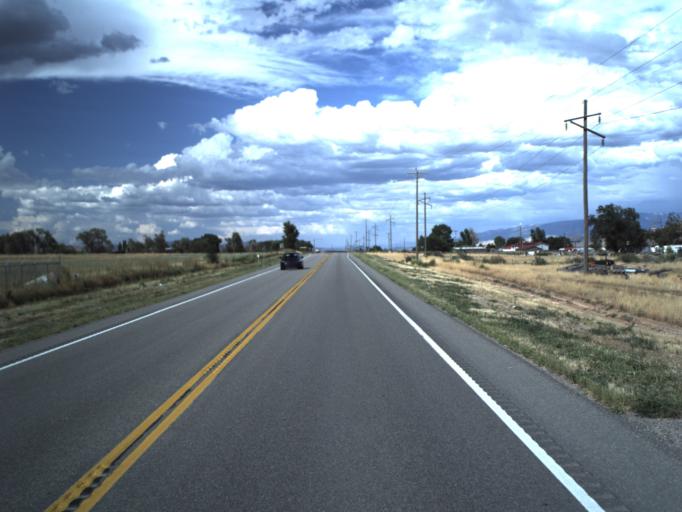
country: US
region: Utah
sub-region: Sevier County
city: Aurora
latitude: 38.8615
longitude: -111.9683
